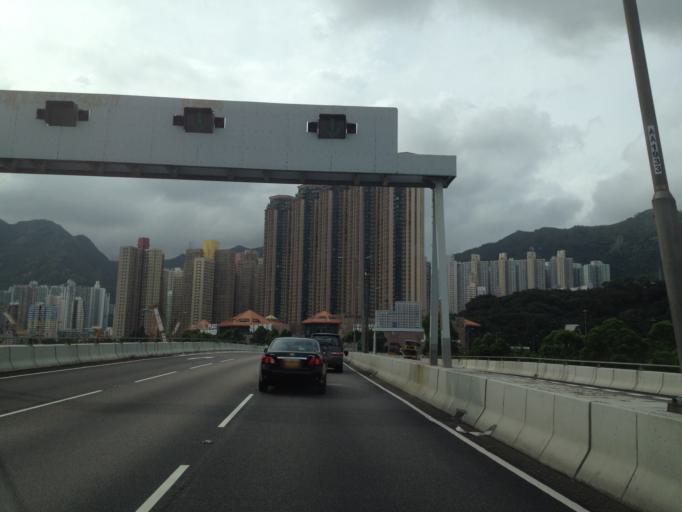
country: HK
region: Wong Tai Sin
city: Wong Tai Sin
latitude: 22.3371
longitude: 114.2039
